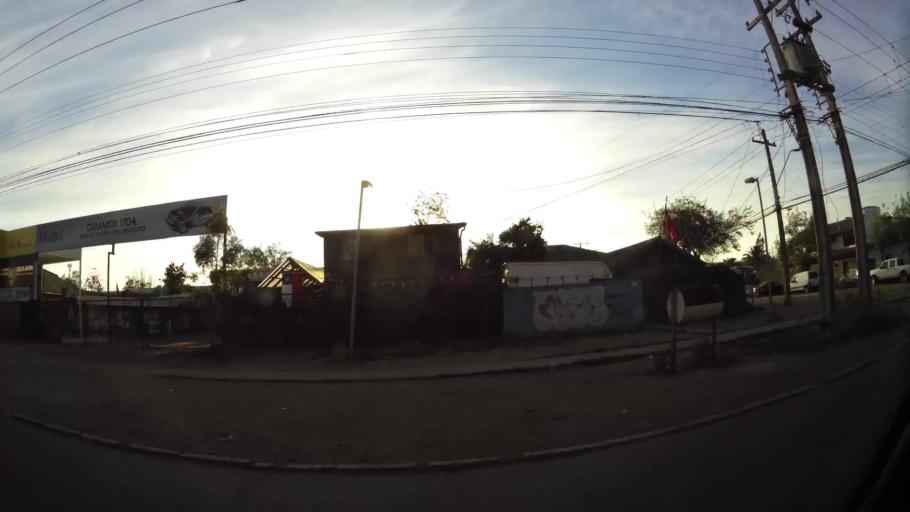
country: CL
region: Santiago Metropolitan
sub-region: Provincia de Santiago
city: Lo Prado
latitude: -33.4270
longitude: -70.7193
